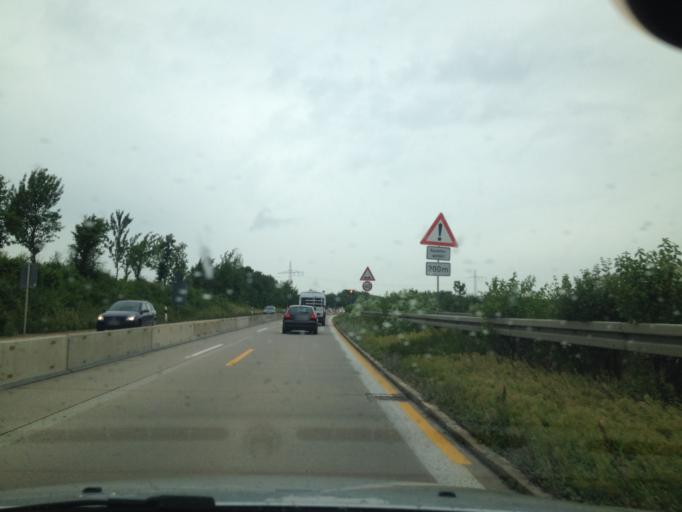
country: DE
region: Bavaria
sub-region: Regierungsbezirk Unterfranken
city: Marktbreit
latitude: 49.6563
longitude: 10.1344
